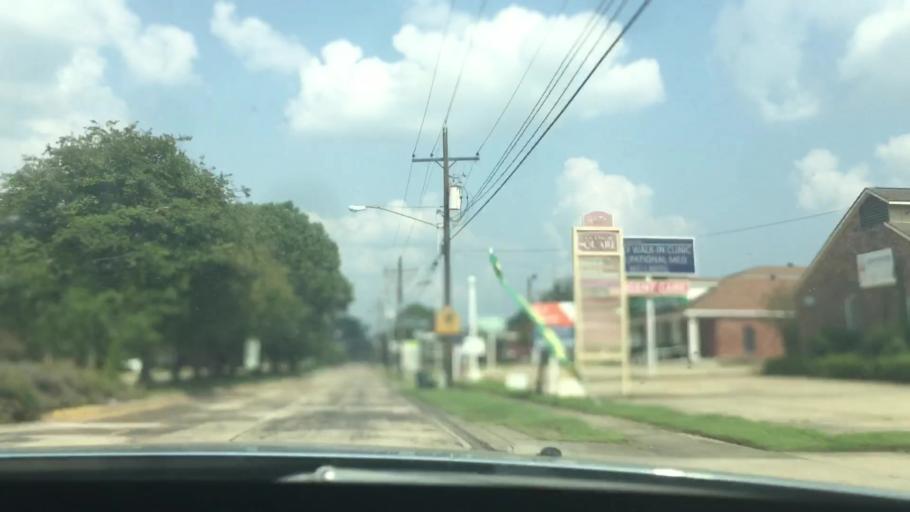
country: US
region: Louisiana
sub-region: East Baton Rouge Parish
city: Westminster
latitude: 30.4425
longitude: -91.1024
